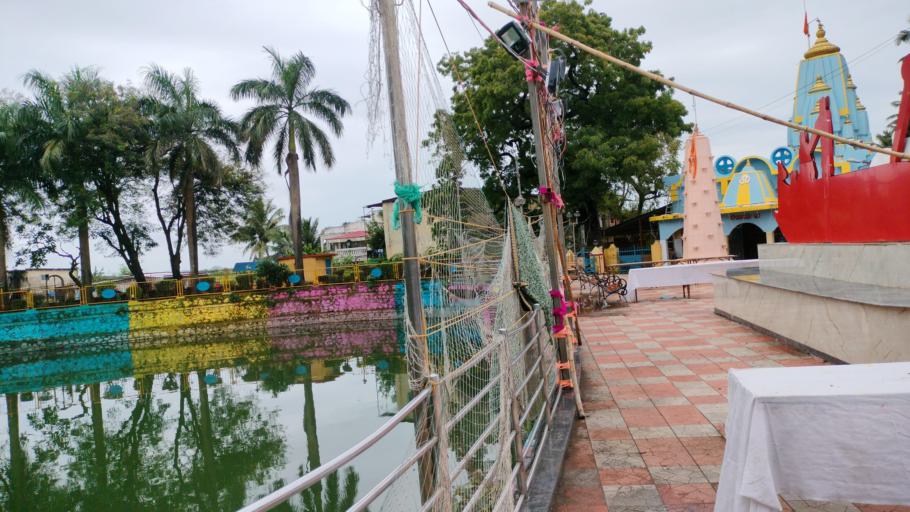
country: IN
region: Maharashtra
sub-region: Thane
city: Bhayandar
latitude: 19.2933
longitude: 72.8205
